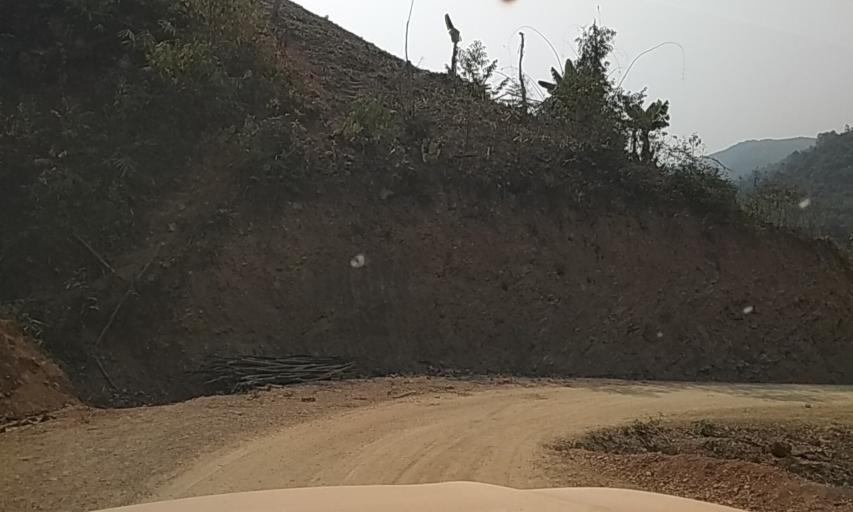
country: LA
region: Phongsali
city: Phongsali
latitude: 21.4711
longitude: 102.4326
